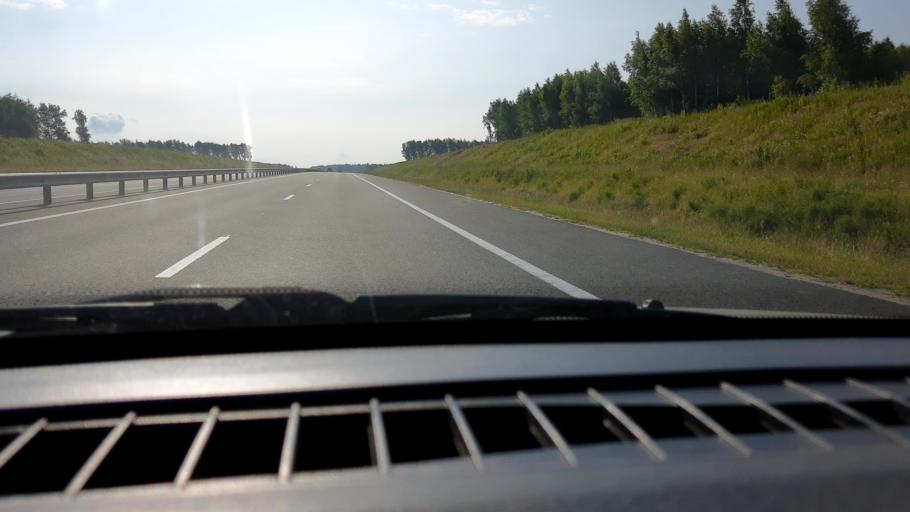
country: RU
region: Nizjnij Novgorod
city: Afonino
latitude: 56.1053
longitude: 43.9978
